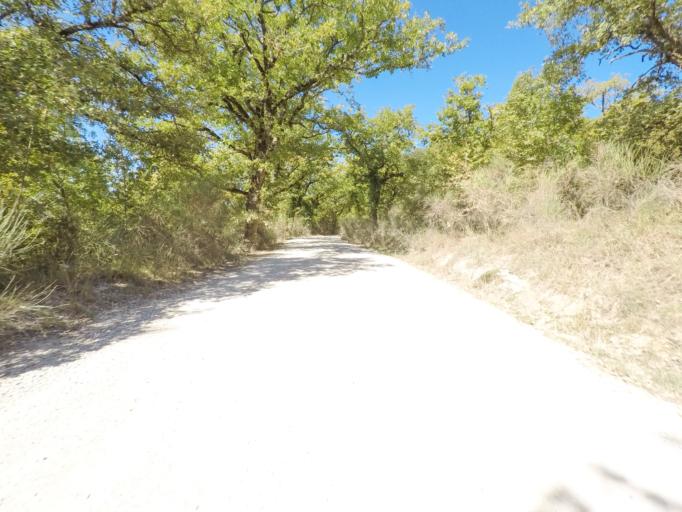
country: IT
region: Tuscany
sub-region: Provincia di Siena
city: Castellina in Chianti
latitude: 43.4291
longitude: 11.3340
